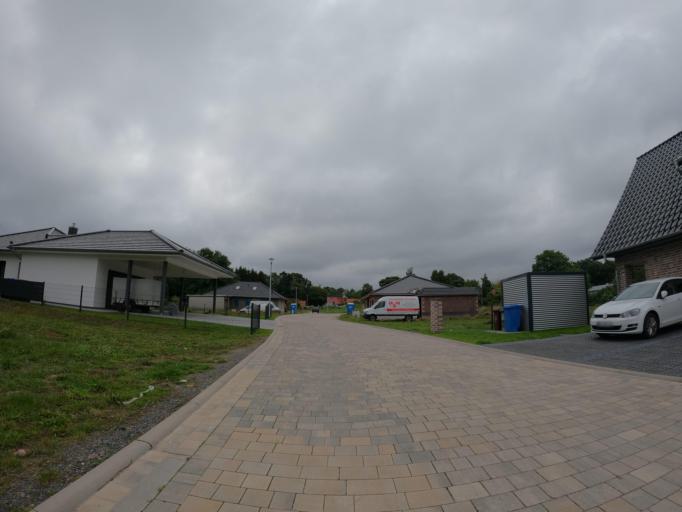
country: DE
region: Mecklenburg-Vorpommern
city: Garz
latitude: 54.3243
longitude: 13.3529
